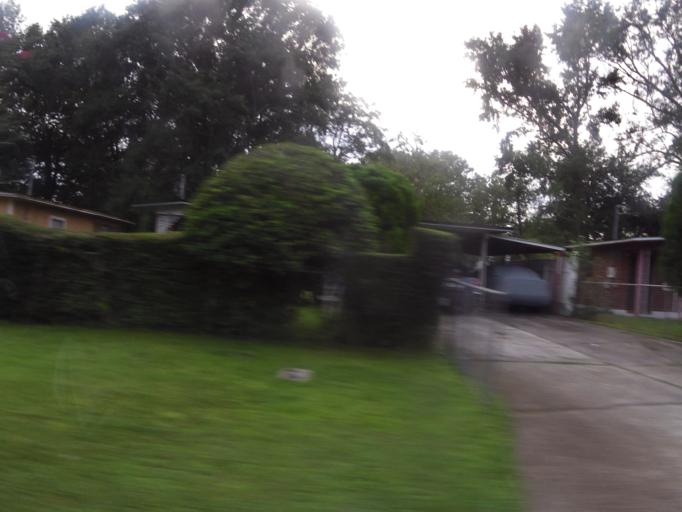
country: US
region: Florida
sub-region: Duval County
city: Jacksonville
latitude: 30.3590
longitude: -81.7085
